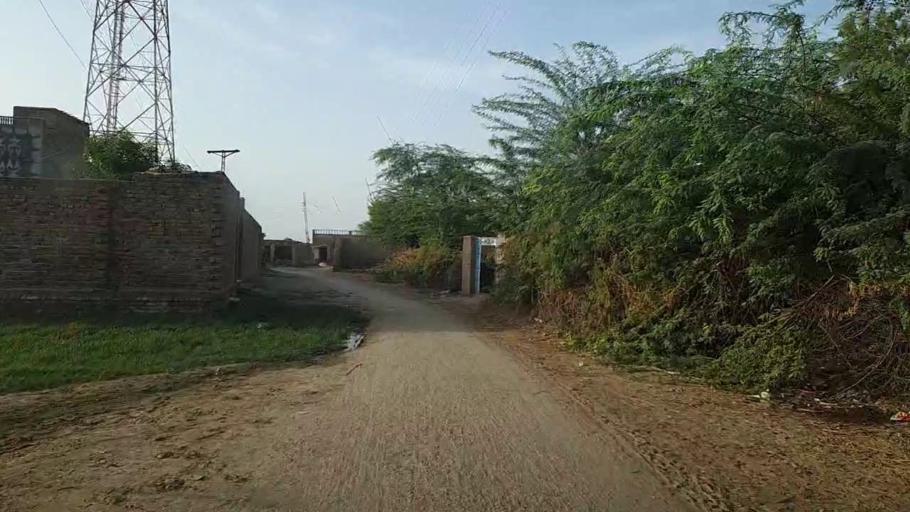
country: PK
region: Sindh
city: Bhiria
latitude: 26.9104
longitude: 68.2639
